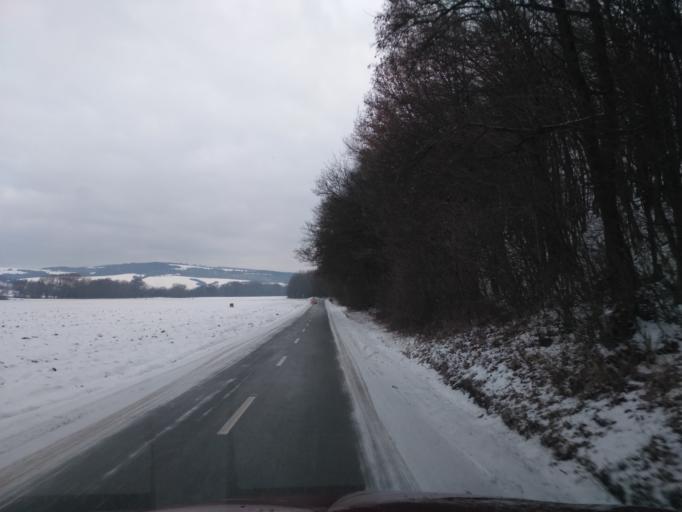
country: SK
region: Presovsky
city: Sabinov
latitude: 49.0520
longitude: 21.0900
